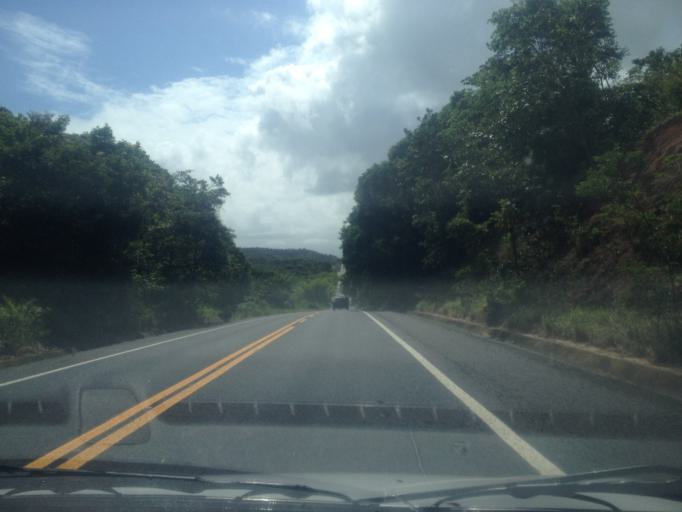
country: BR
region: Sergipe
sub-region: Indiaroba
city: Indiaroba
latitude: -11.6056
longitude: -37.5397
